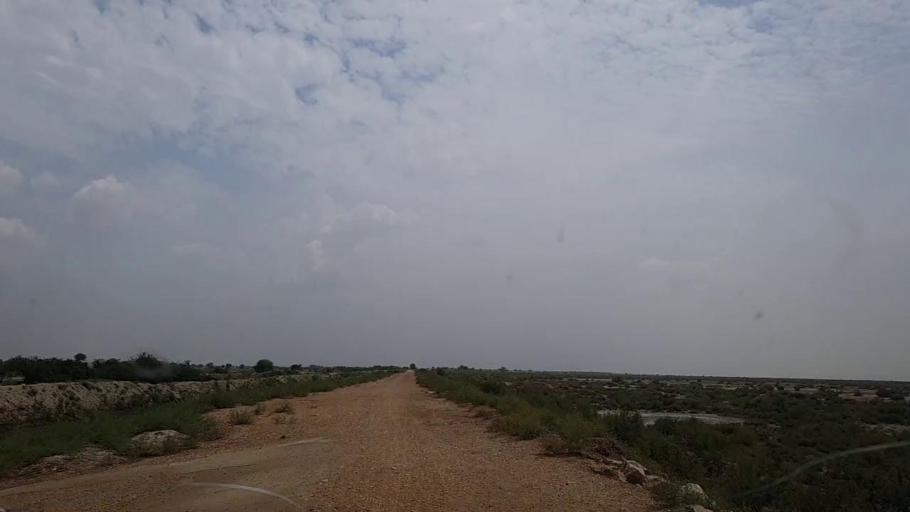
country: PK
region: Sindh
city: Phulji
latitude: 26.8388
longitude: 67.6179
